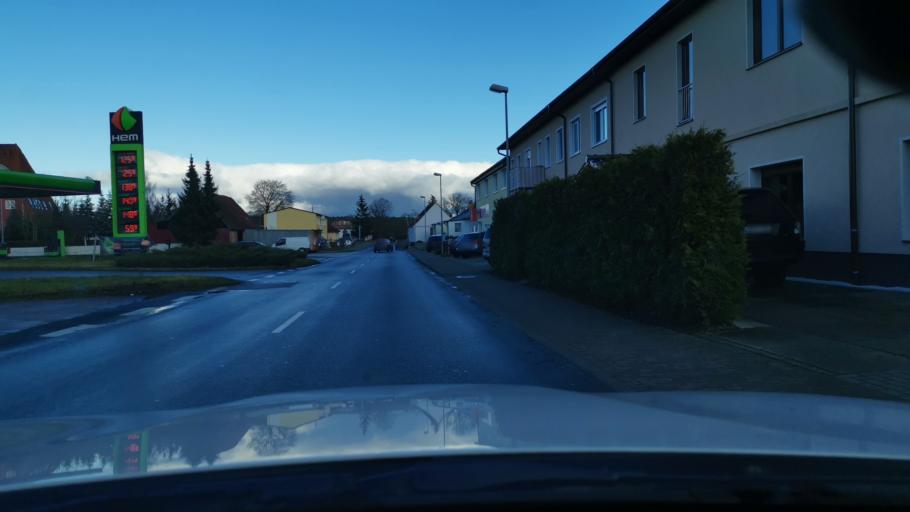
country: DE
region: Mecklenburg-Vorpommern
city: Tessin
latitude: 54.0301
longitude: 12.4701
